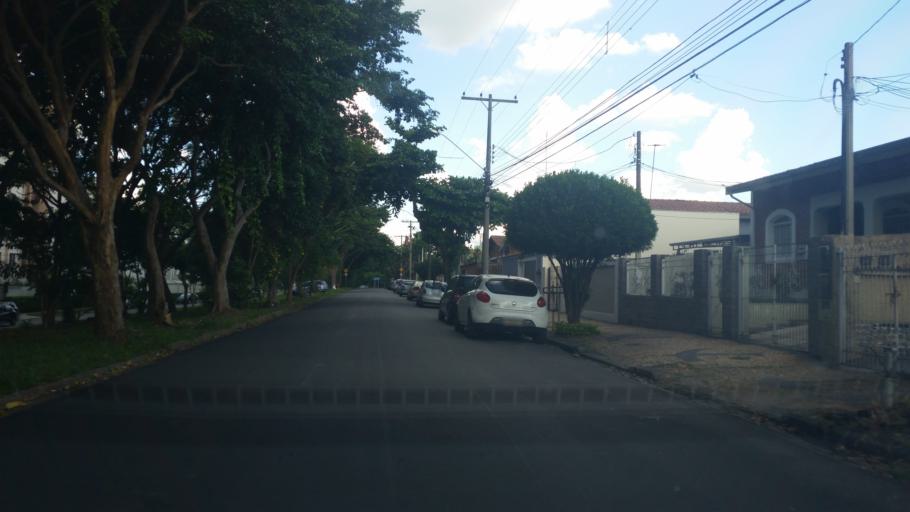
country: BR
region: Sao Paulo
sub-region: Campinas
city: Campinas
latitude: -22.8836
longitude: -47.0285
